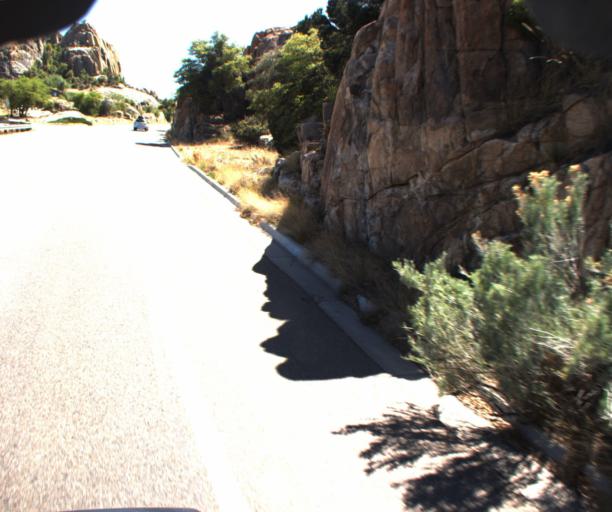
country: US
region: Arizona
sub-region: Yavapai County
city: Prescott
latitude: 34.6113
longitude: -112.4191
